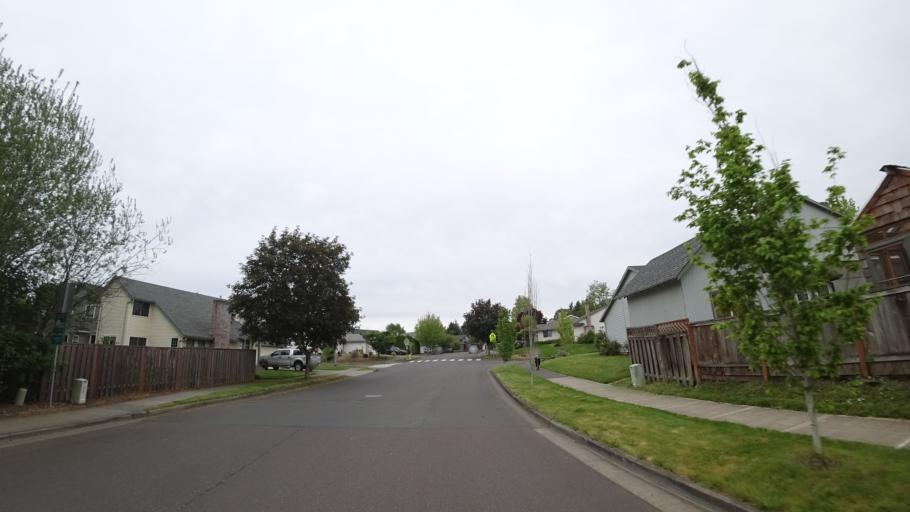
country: US
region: Oregon
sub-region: Washington County
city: Aloha
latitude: 45.5067
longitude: -122.9068
